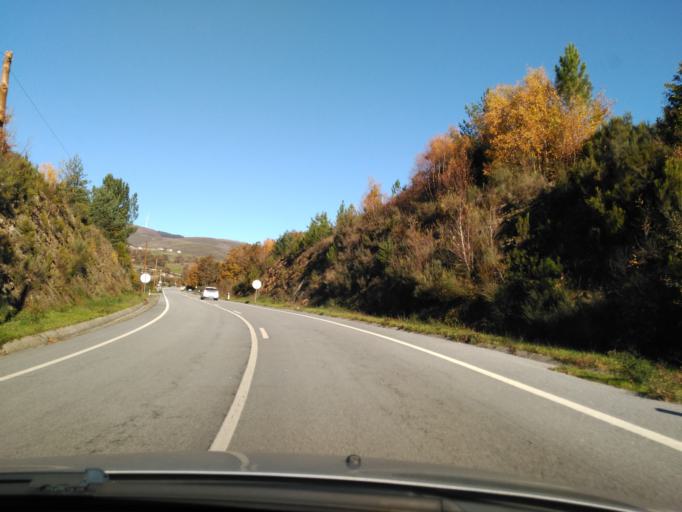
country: PT
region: Braga
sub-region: Cabeceiras de Basto
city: Cabeceiras de Basto
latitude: 41.6954
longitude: -7.9381
